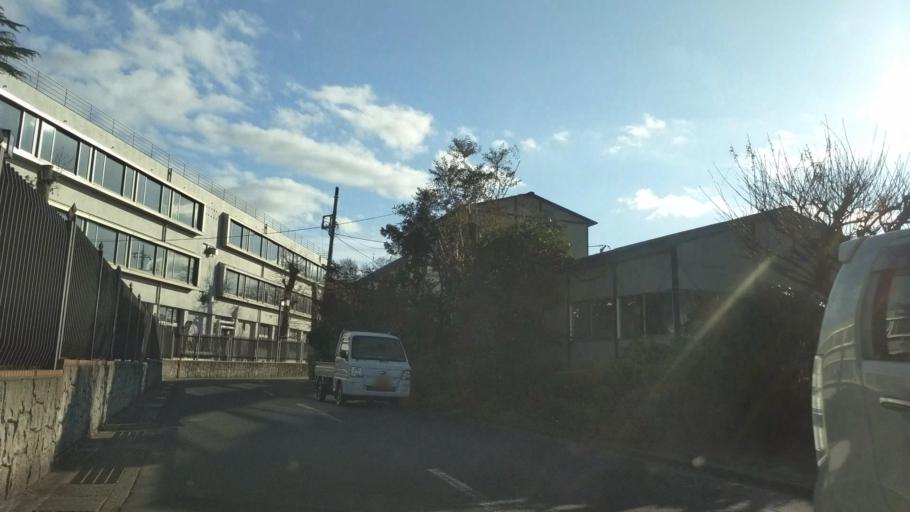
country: JP
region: Kanagawa
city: Isehara
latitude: 35.3615
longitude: 139.2707
